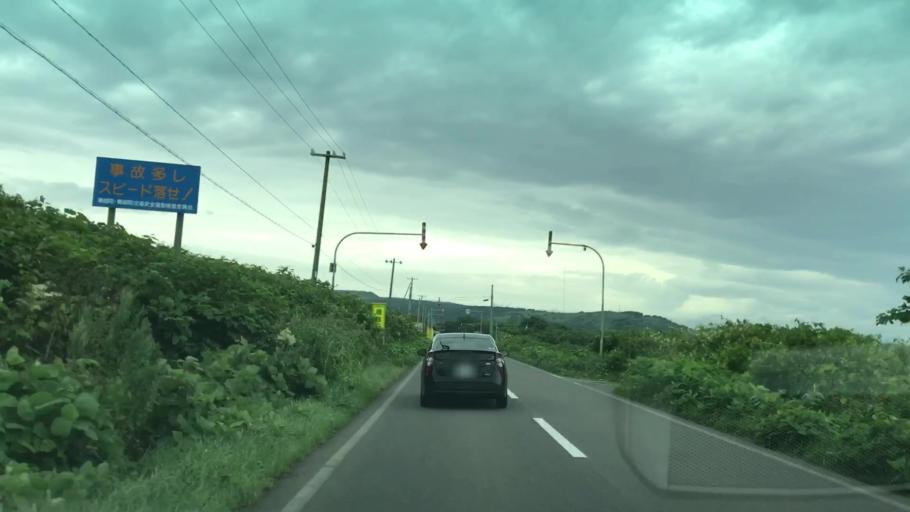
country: JP
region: Hokkaido
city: Iwanai
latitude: 42.8935
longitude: 140.3766
